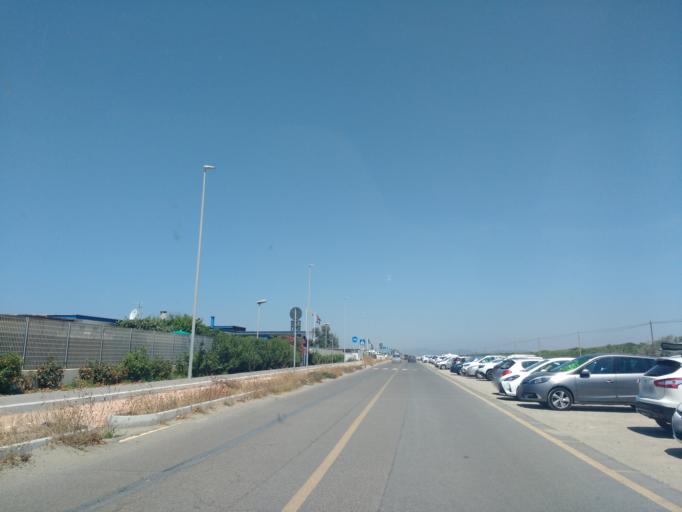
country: IT
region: Latium
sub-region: Citta metropolitana di Roma Capitale
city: Passo Oscuro
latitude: 41.8788
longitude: 12.1756
